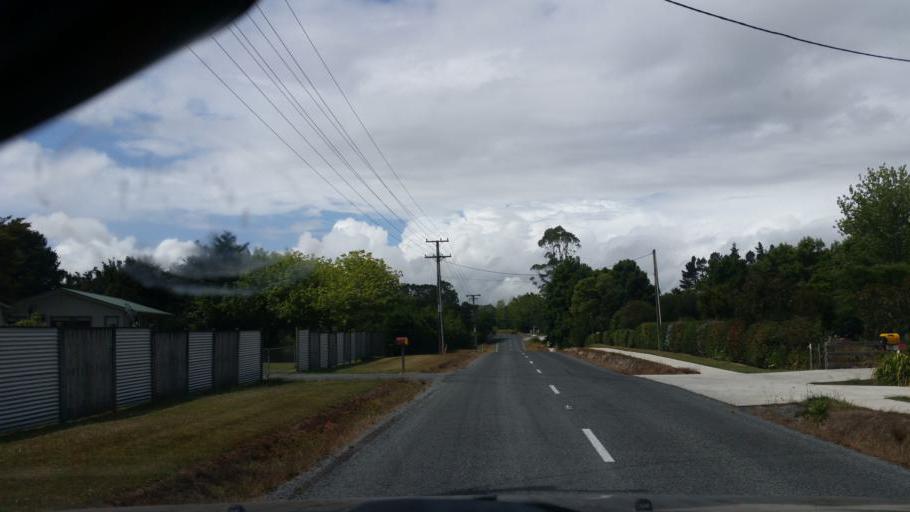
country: NZ
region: Auckland
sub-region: Auckland
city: Wellsford
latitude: -36.1255
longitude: 174.5595
